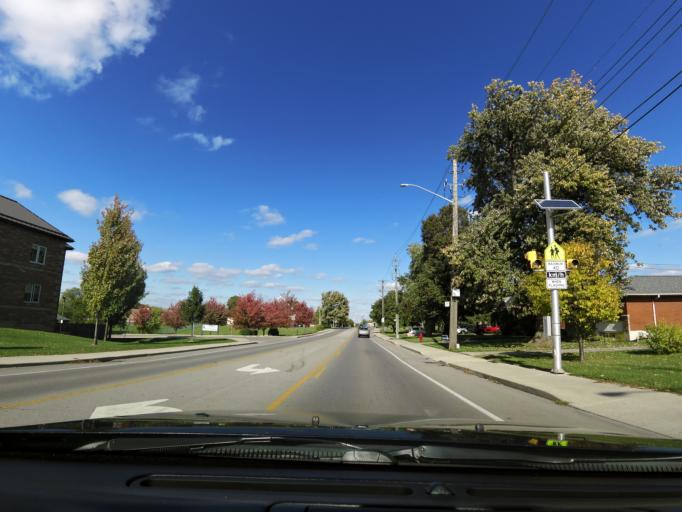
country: CA
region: Ontario
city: Hamilton
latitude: 43.2309
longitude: -79.9128
